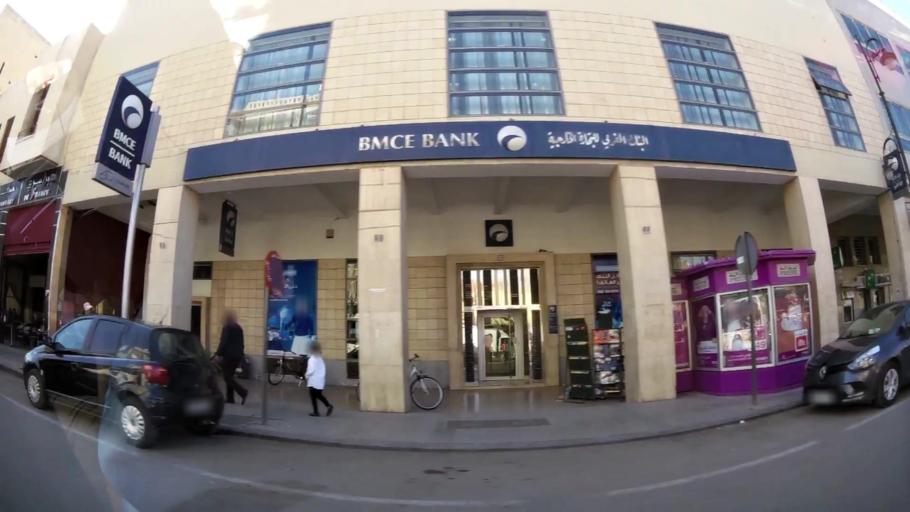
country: MA
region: Oriental
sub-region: Oujda-Angad
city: Oujda
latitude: 34.6826
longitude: -1.9164
